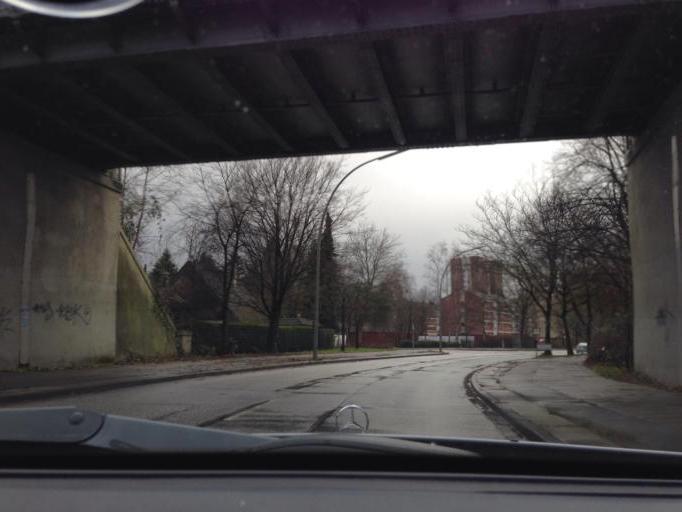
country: DE
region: Hamburg
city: Farmsen-Berne
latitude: 53.5959
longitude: 10.0922
